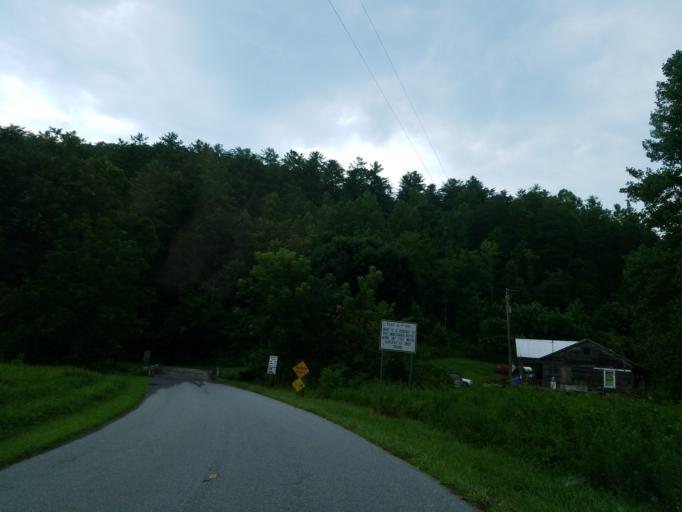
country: US
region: Georgia
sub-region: Fannin County
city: Blue Ridge
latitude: 34.7776
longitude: -84.3811
